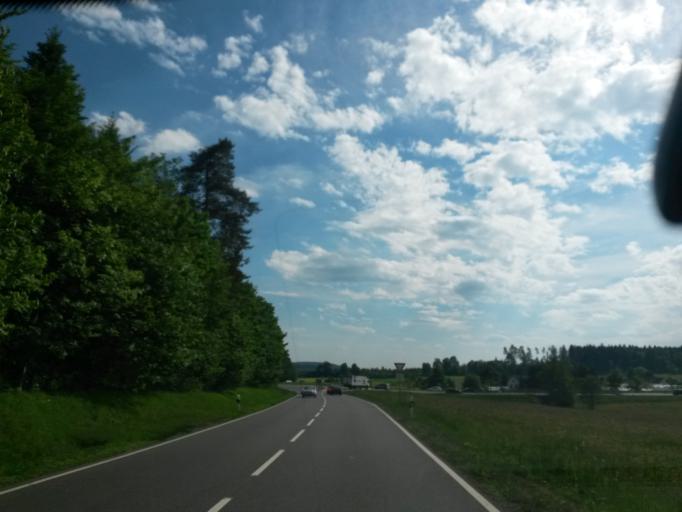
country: DE
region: Baden-Wuerttemberg
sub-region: Karlsruhe Region
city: Althengstett
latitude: 48.7370
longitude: 8.7914
